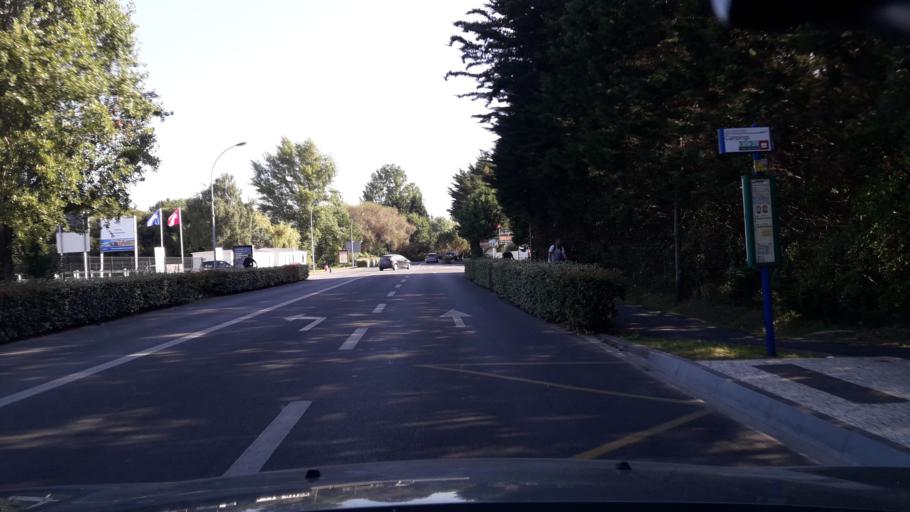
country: FR
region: Poitou-Charentes
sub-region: Departement de la Charente-Maritime
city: Les Mathes
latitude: 45.7134
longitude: -1.1597
